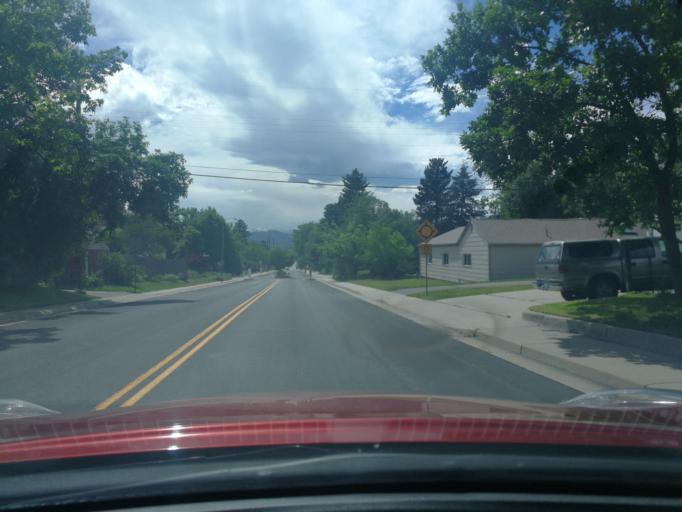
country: US
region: Colorado
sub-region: Arapahoe County
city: Littleton
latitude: 39.6151
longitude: -105.0020
